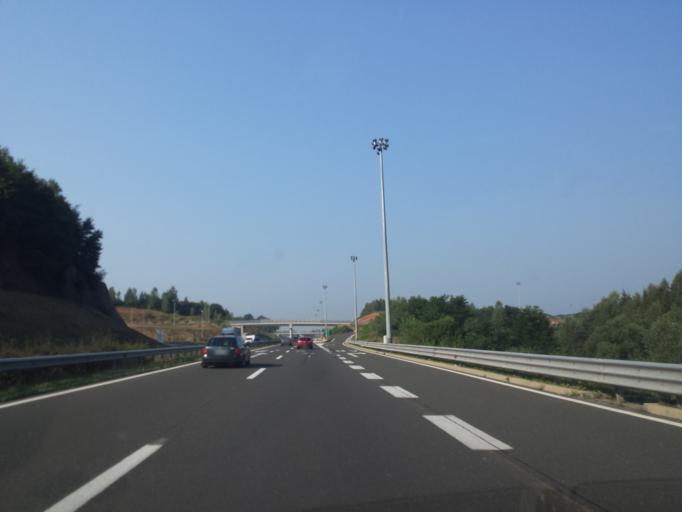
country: HR
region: Karlovacka
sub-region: Grad Karlovac
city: Karlovac
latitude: 45.4815
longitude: 15.4317
